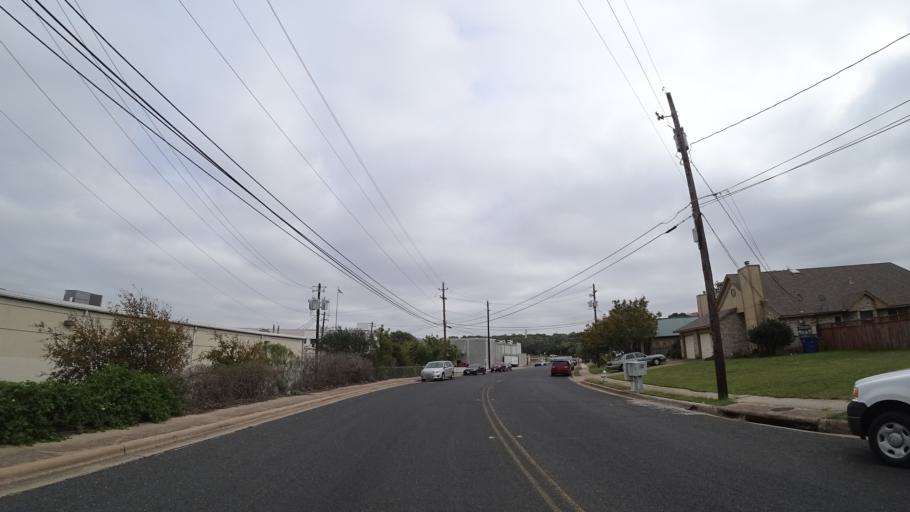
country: US
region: Texas
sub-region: Travis County
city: Barton Creek
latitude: 30.2340
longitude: -97.8780
